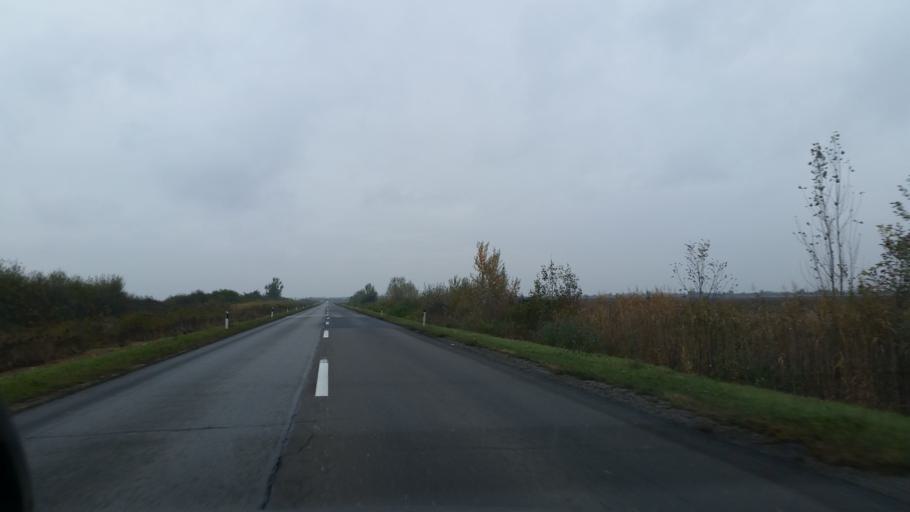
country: RS
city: Sefkerin
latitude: 44.9597
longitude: 20.4245
